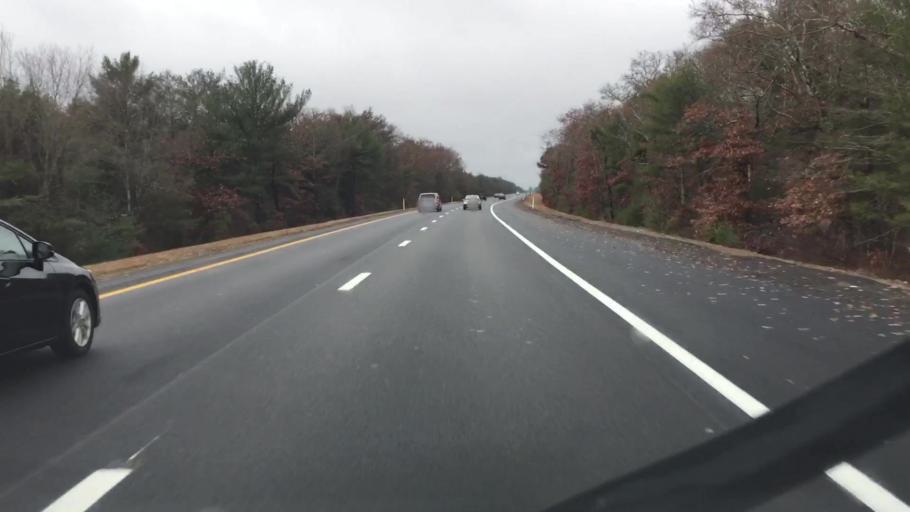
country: US
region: Massachusetts
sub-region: Plymouth County
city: Wareham Center
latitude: 41.7858
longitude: -70.7363
